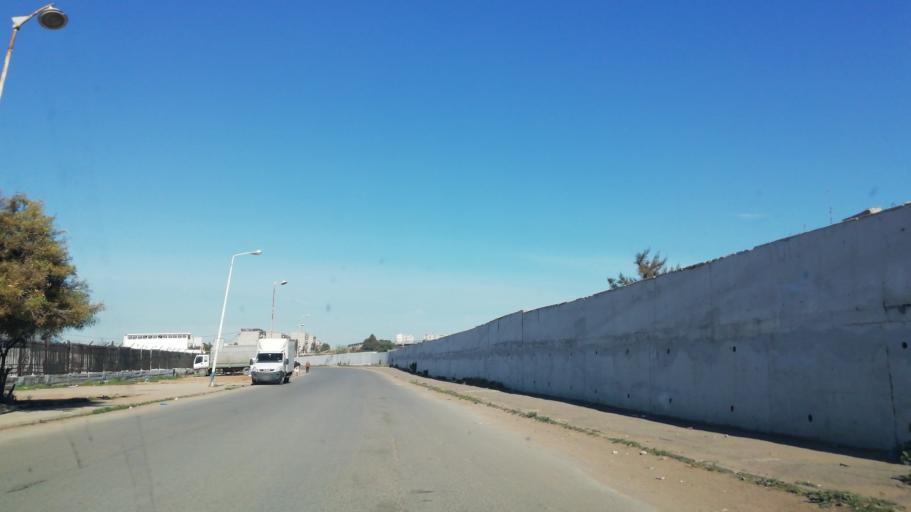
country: DZ
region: Oran
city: Oran
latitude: 35.6856
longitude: -0.6296
